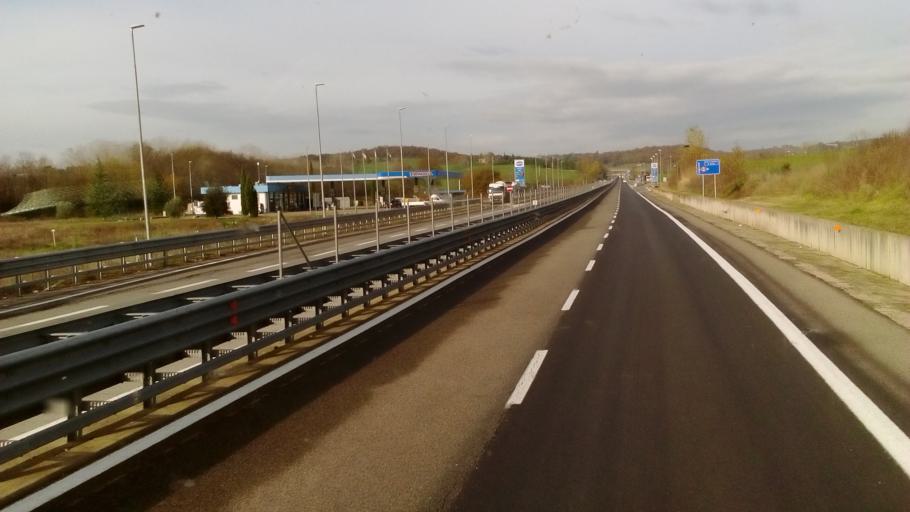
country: IT
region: Tuscany
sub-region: Provincia di Siena
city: Rapolano Terme
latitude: 43.3222
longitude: 11.5674
